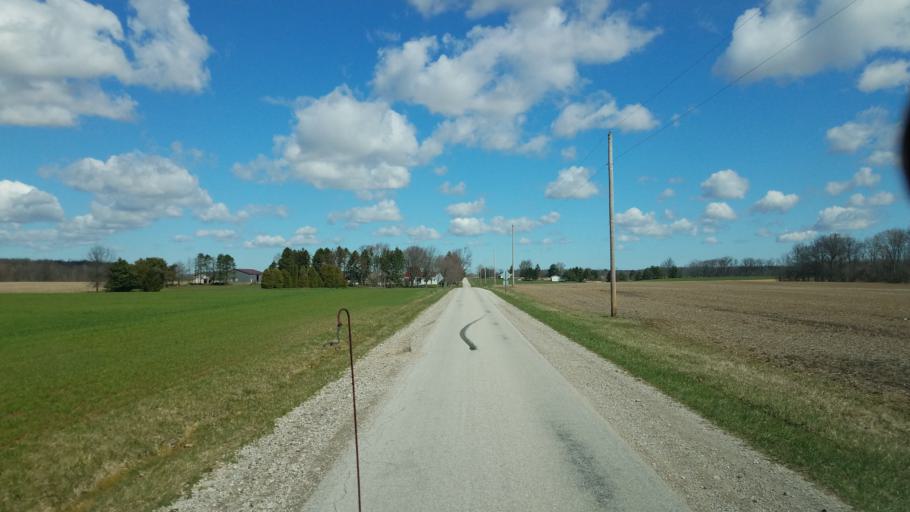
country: US
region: Ohio
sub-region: Sandusky County
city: Mount Carmel
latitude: 41.1113
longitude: -82.9383
